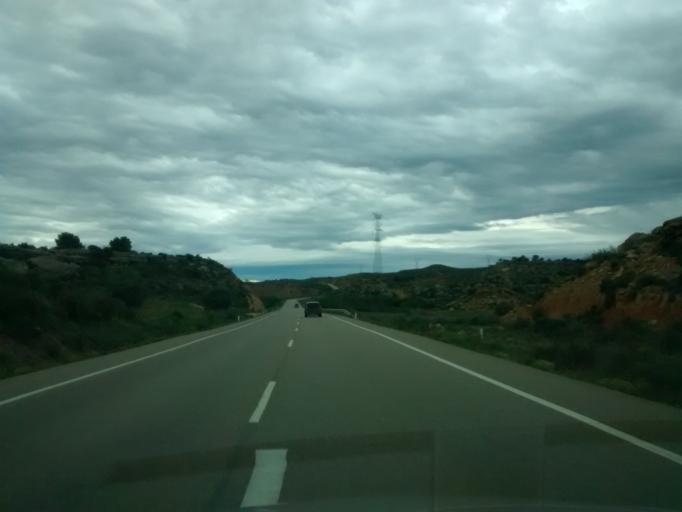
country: ES
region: Aragon
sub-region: Provincia de Zaragoza
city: Caspe
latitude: 41.1921
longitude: 0.0458
